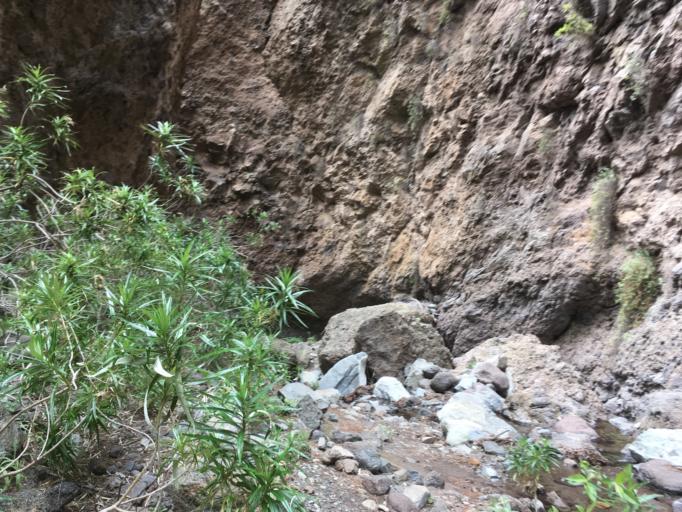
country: ES
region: Canary Islands
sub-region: Provincia de Santa Cruz de Tenerife
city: Vilaflor
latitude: 28.1979
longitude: -16.5756
